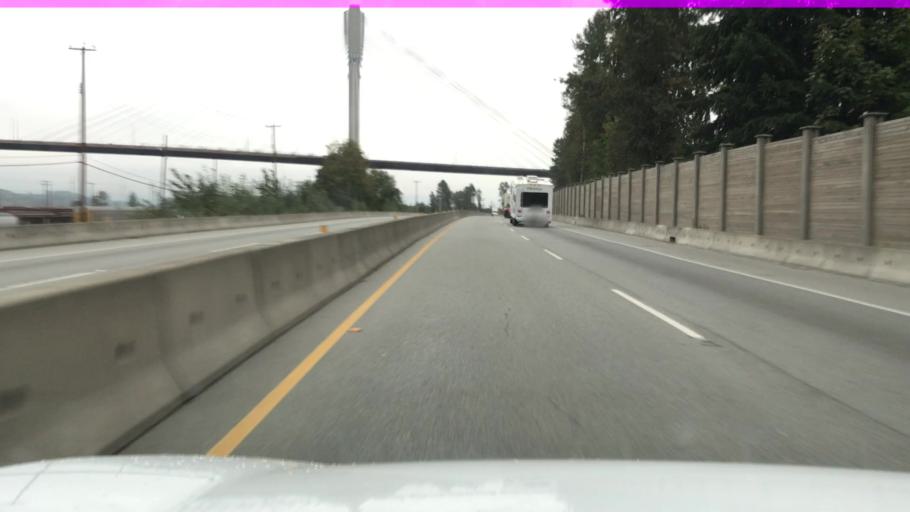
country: CA
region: British Columbia
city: Port Moody
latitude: 49.2145
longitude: -122.8205
